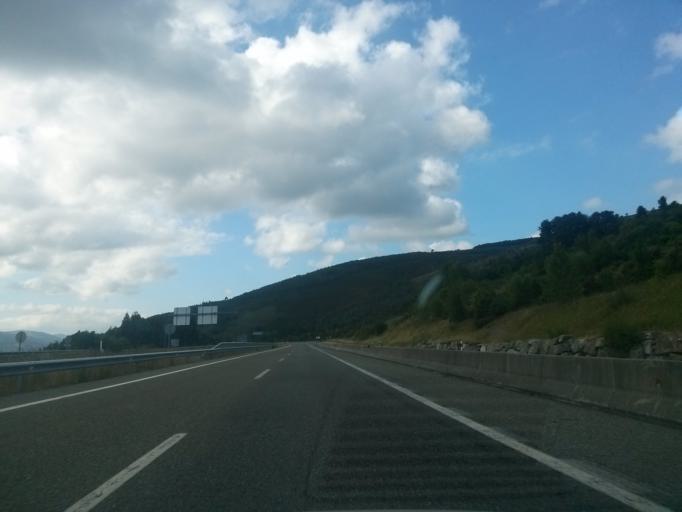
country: ES
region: Galicia
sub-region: Provincia de Lugo
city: Becerrea
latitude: 42.8810
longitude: -7.1765
